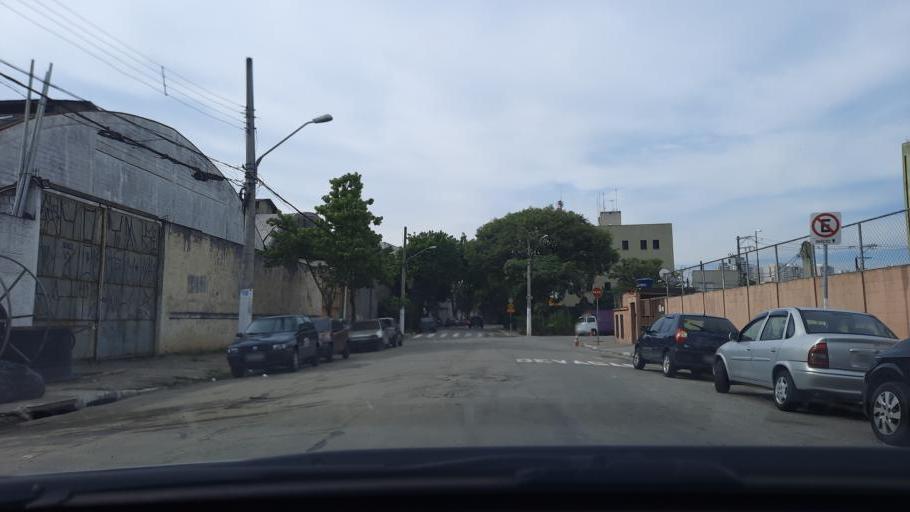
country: BR
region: Sao Paulo
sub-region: Sao Paulo
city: Sao Paulo
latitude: -23.5051
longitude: -46.6836
